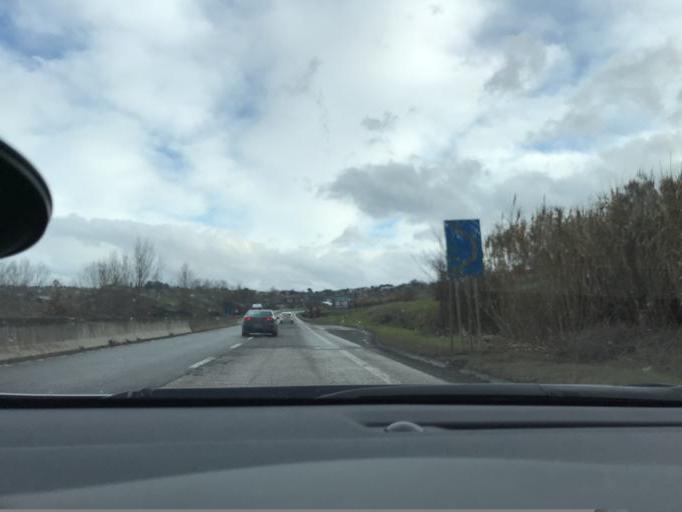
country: IT
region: Umbria
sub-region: Provincia di Perugia
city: Via Lippia
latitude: 43.1047
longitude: 12.4854
